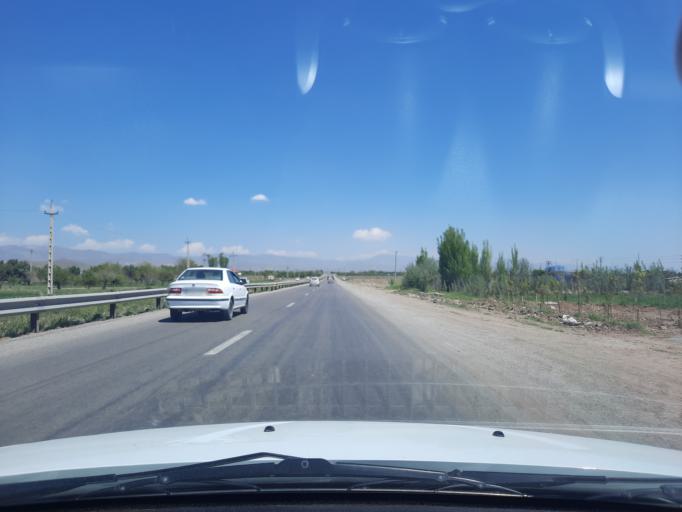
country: IR
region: Qazvin
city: Qazvin
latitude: 36.2636
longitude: 50.0589
